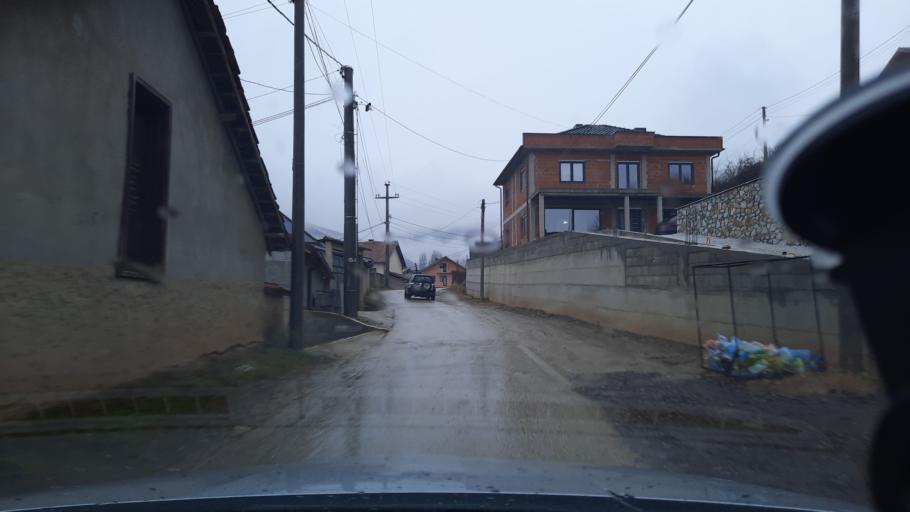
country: MK
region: Opstina Lipkovo
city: Otlja
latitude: 42.1448
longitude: 21.5821
